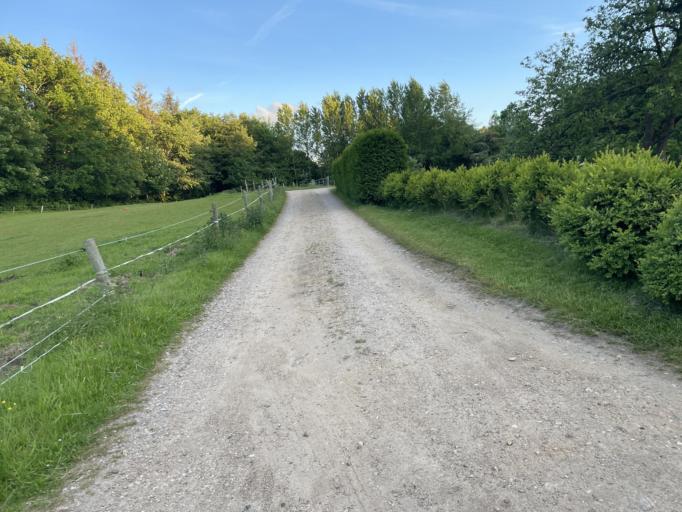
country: DE
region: Schleswig-Holstein
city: Husum
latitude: 54.4723
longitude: 9.0717
